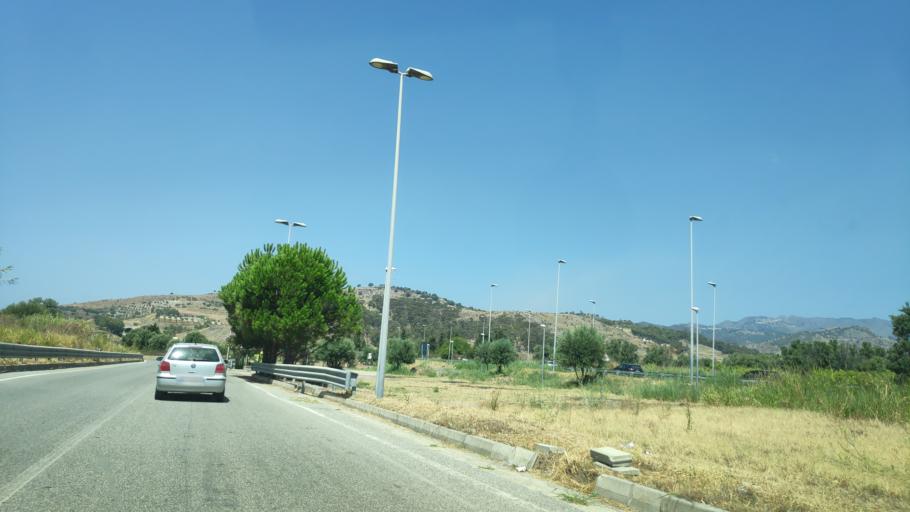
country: IT
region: Calabria
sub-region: Provincia di Reggio Calabria
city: Palizzi Marina
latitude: 37.9224
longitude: 15.9550
